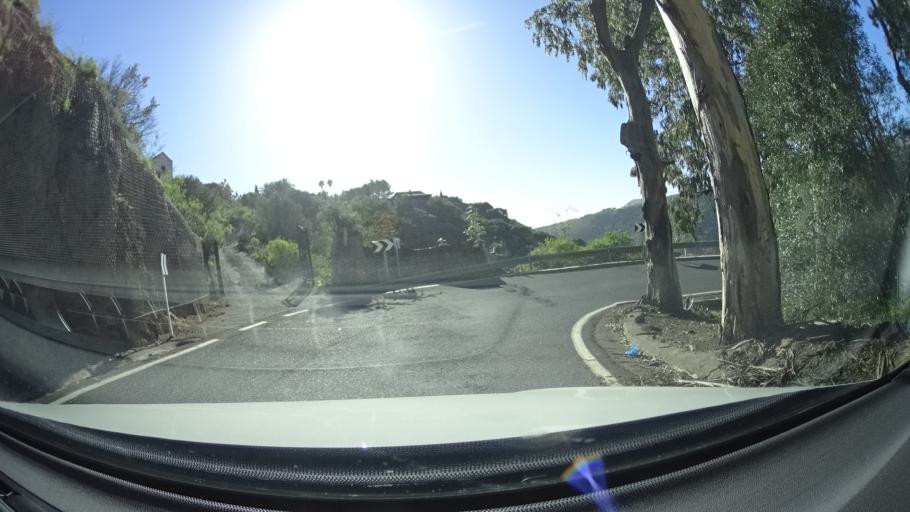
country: ES
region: Canary Islands
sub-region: Provincia de Las Palmas
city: Santa Brigida
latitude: 28.0287
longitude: -15.4712
